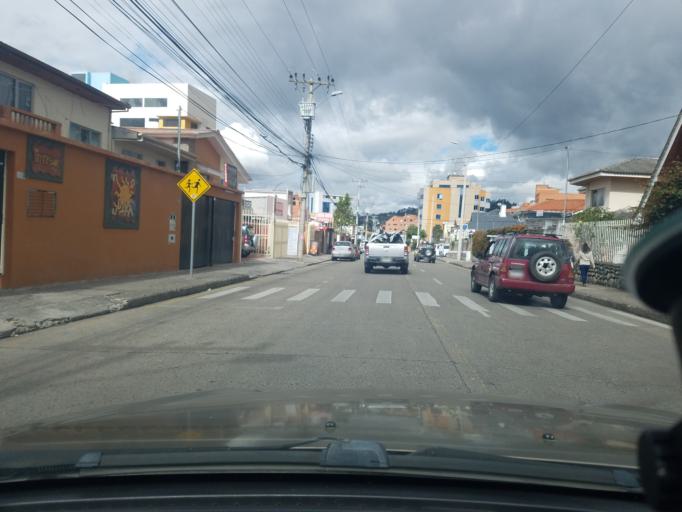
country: EC
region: Azuay
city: Cuenca
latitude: -2.9088
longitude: -79.0017
